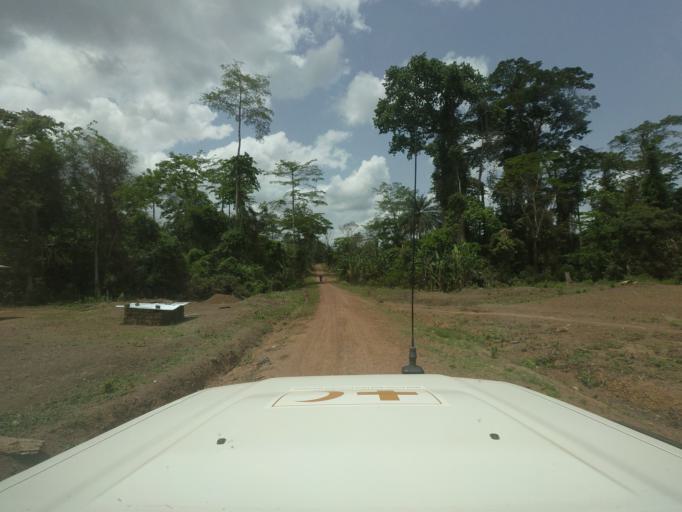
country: GN
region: Nzerekore
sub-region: Yomou
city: Yomou
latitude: 7.2816
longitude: -9.1836
